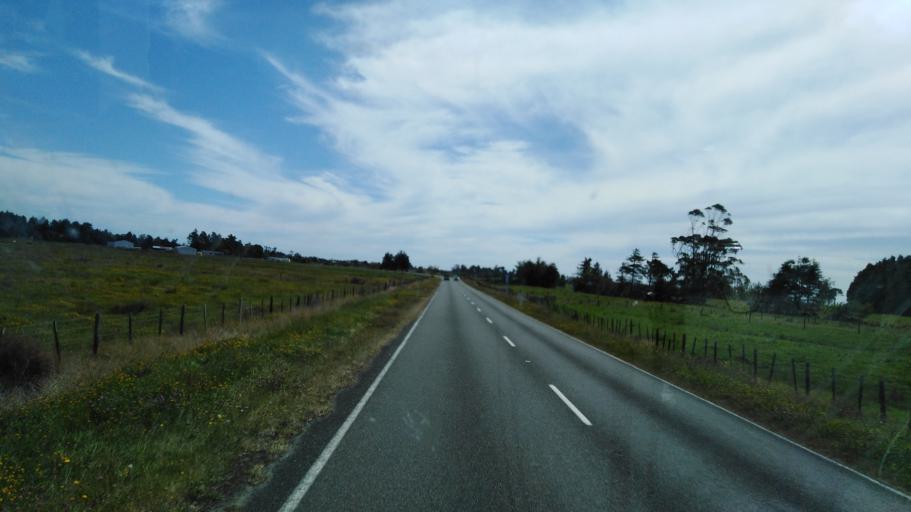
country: NZ
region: West Coast
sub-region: Buller District
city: Westport
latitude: -41.7584
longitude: 171.6424
